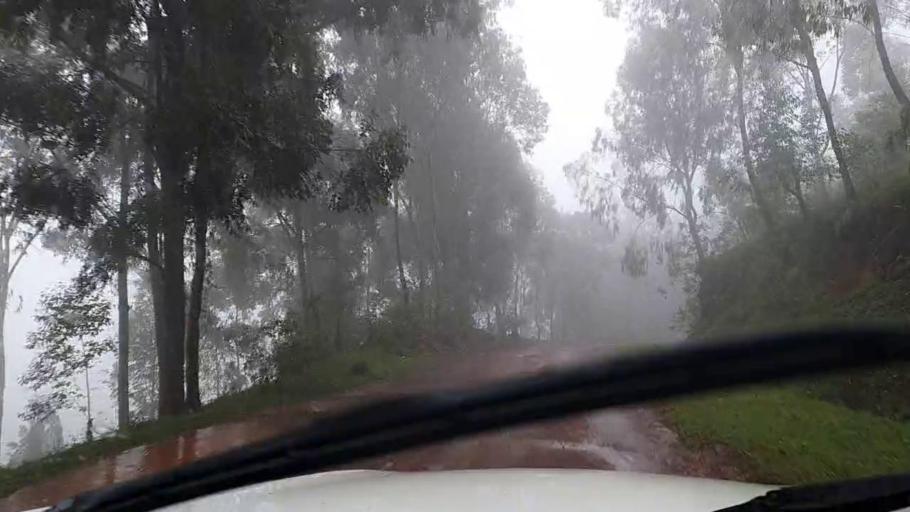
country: RW
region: Kigali
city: Kigali
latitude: -1.7671
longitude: 29.9942
